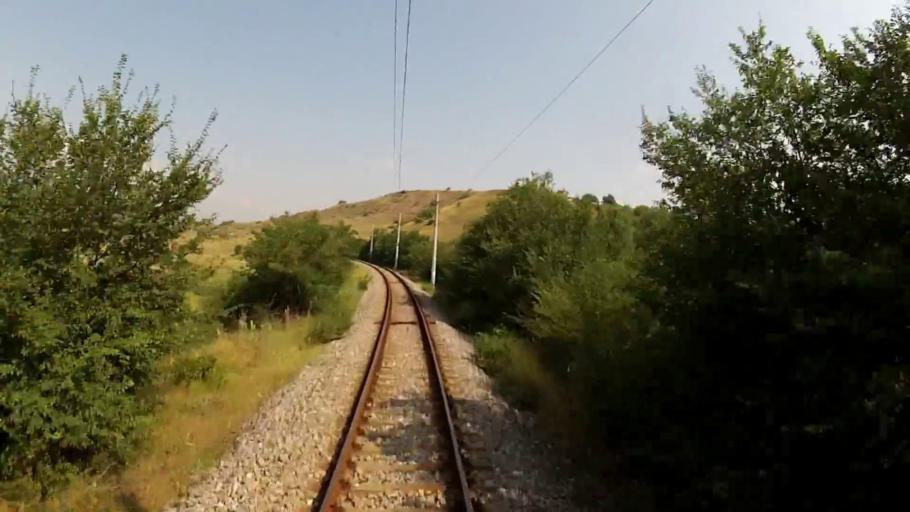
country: BG
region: Blagoevgrad
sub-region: Obshtina Sandanski
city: Sandanski
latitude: 41.5225
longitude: 23.2670
